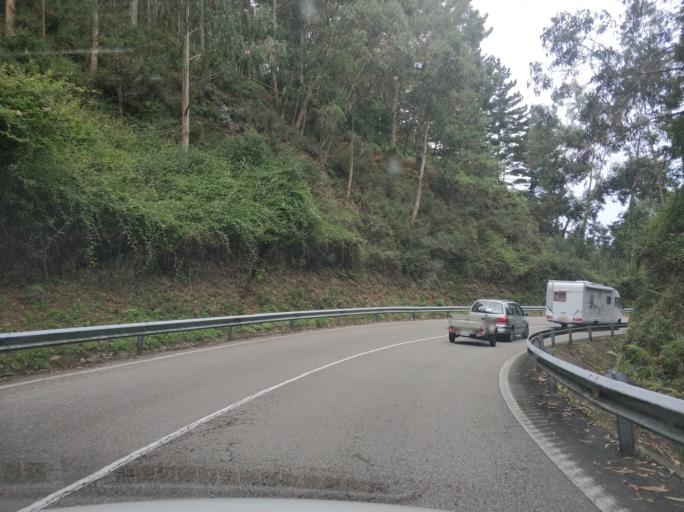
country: ES
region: Asturias
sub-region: Province of Asturias
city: Cudillero
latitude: 43.5648
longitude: -6.1543
